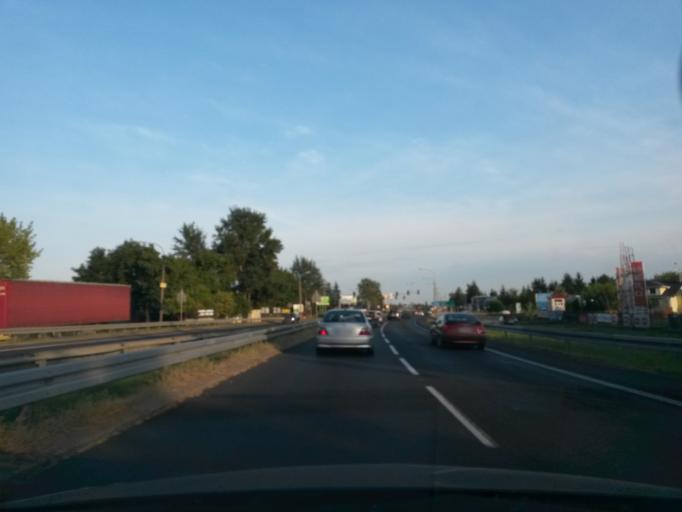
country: PL
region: Masovian Voivodeship
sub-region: Powiat warszawski zachodni
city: Dziekanow Lesny
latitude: 52.3496
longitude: 20.8587
